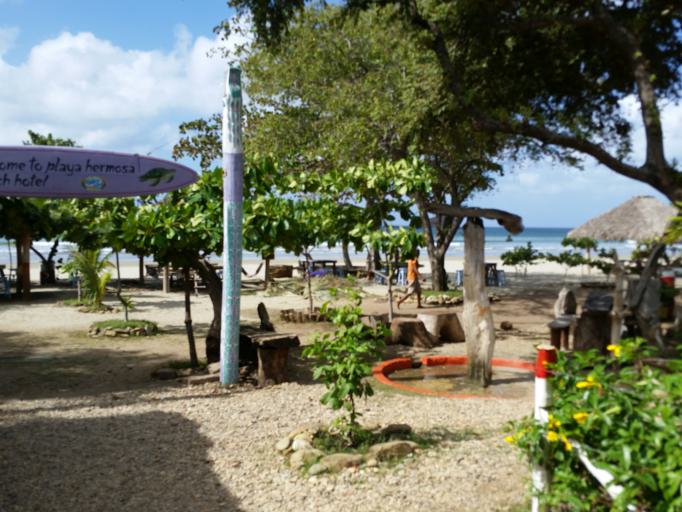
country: NI
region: Rivas
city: San Juan del Sur
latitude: 11.2058
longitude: -85.8350
